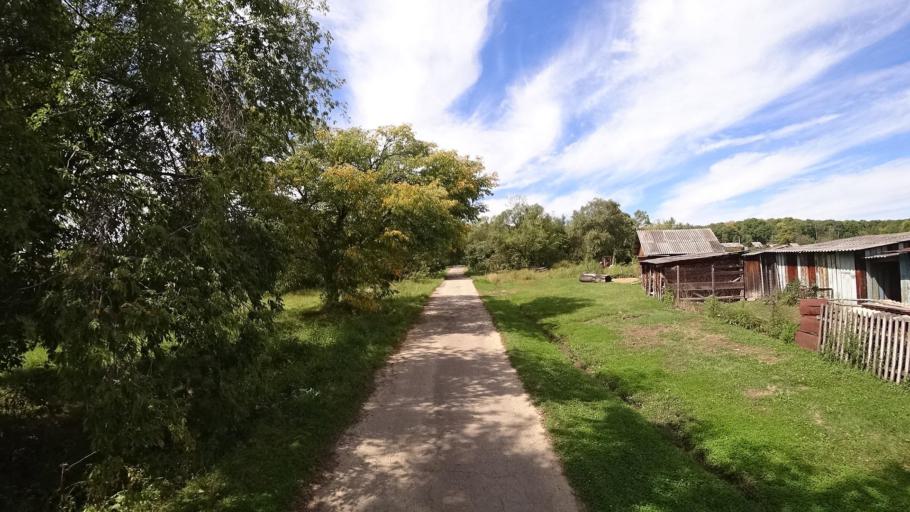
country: RU
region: Primorskiy
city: Yakovlevka
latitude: 44.6465
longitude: 133.5963
